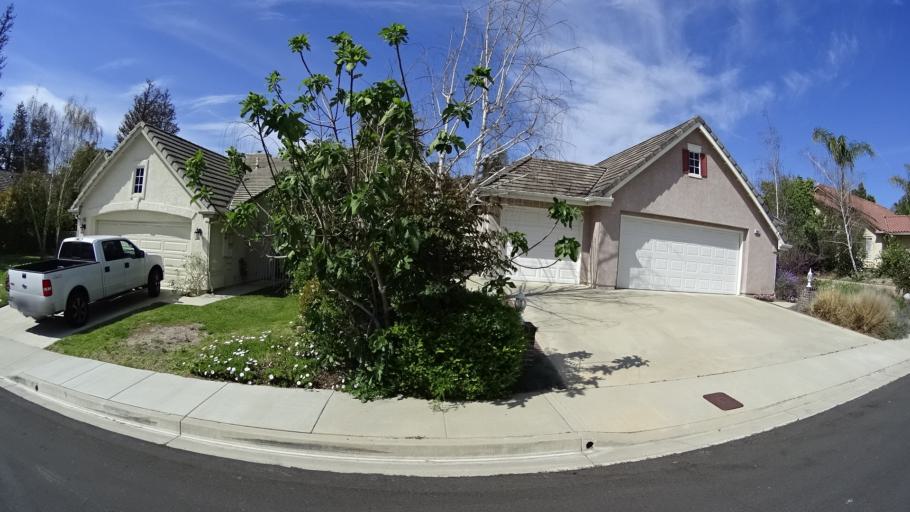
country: US
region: California
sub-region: Ventura County
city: Thousand Oaks
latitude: 34.2173
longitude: -118.8359
